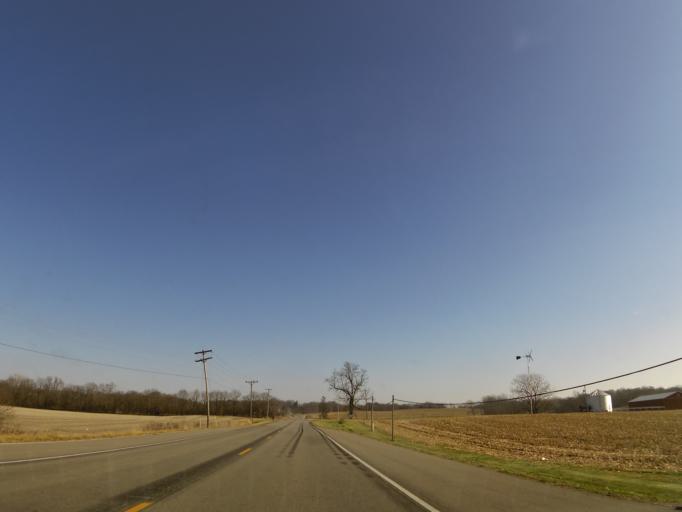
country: US
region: Indiana
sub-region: Fayette County
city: Connersville
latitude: 39.6392
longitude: -85.0770
